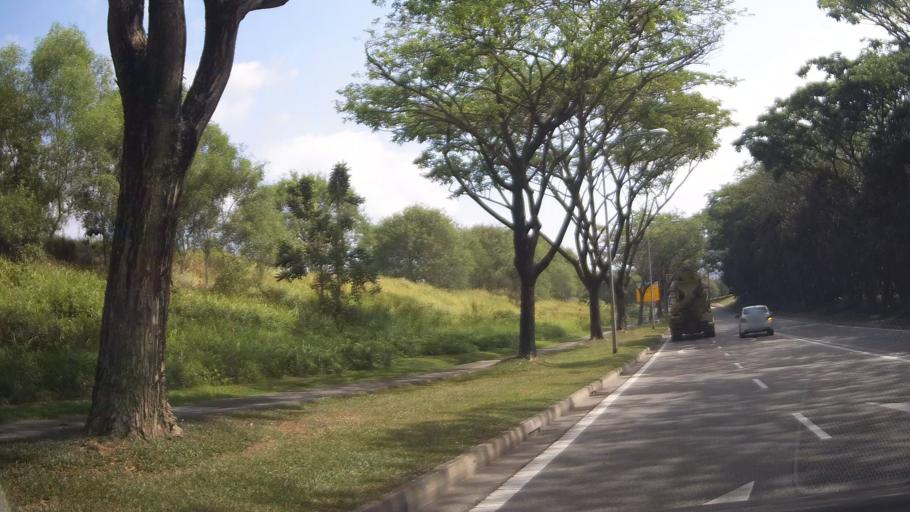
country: SG
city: Singapore
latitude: 1.3637
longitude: 103.9050
